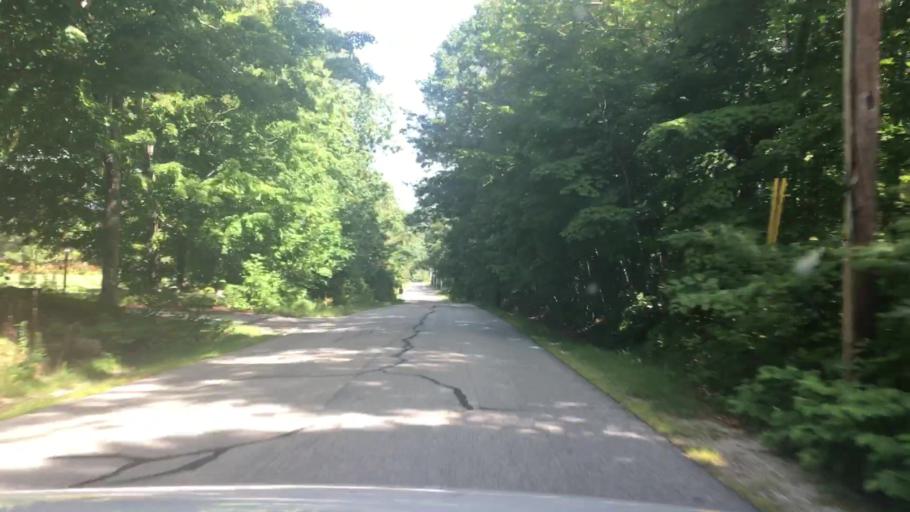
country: US
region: Maine
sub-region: Androscoggin County
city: Turner
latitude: 44.1898
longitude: -70.2601
